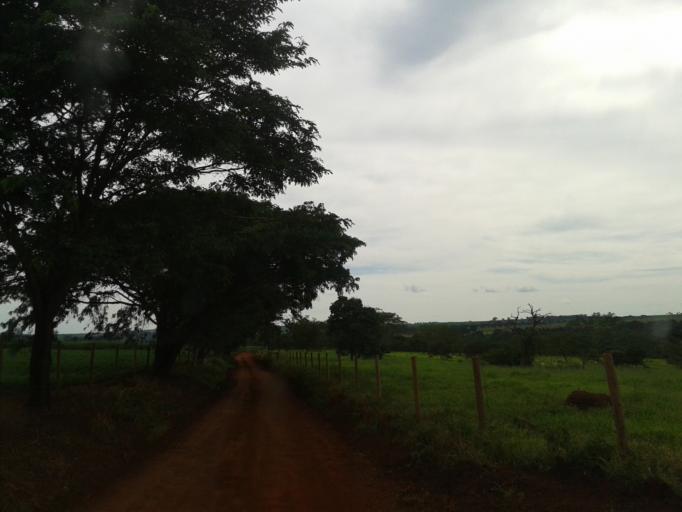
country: BR
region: Minas Gerais
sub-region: Centralina
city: Centralina
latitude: -18.6864
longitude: -49.3638
